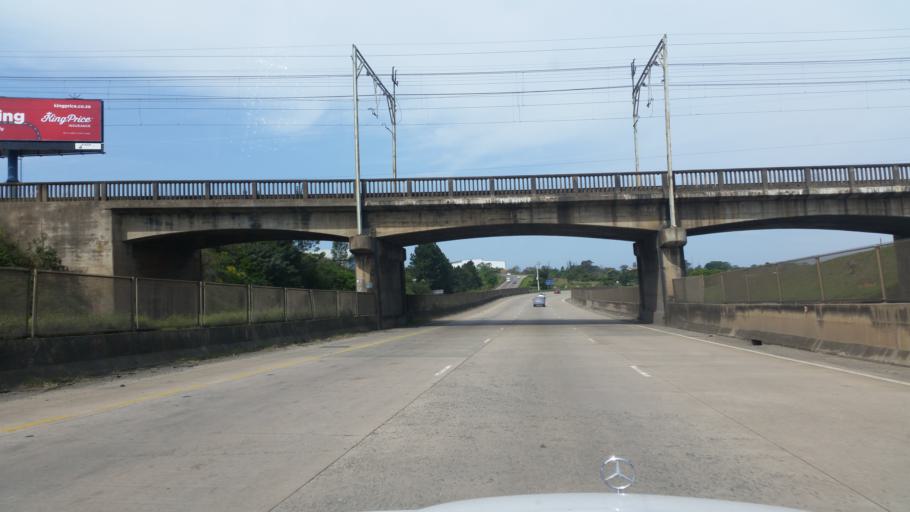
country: ZA
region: KwaZulu-Natal
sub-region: uMgungundlovu District Municipality
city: Camperdown
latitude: -29.7321
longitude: 30.5949
